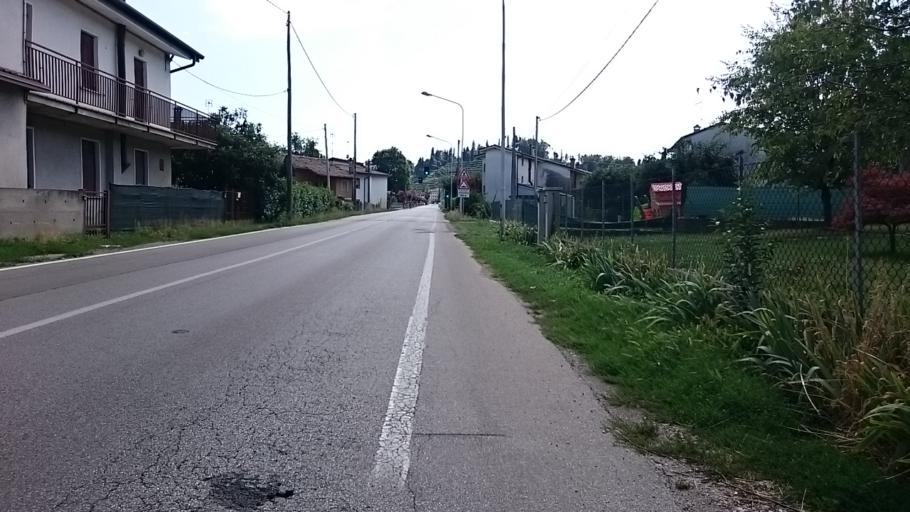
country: IT
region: Veneto
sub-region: Provincia di Treviso
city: Vidor
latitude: 45.8677
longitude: 12.0434
